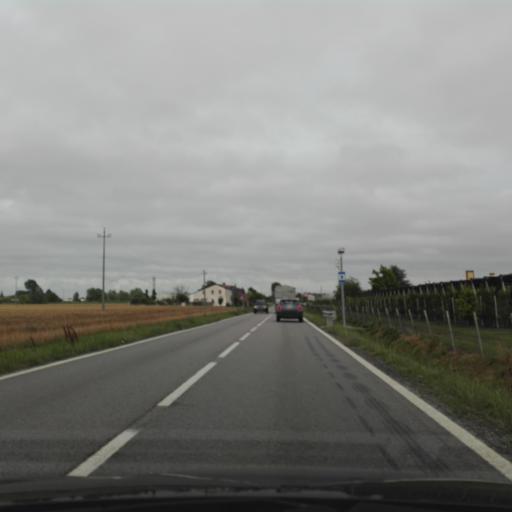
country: IT
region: Veneto
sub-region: Provincia di Rovigo
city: Villanova del Ghebbo Canton
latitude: 45.0771
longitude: 11.6327
